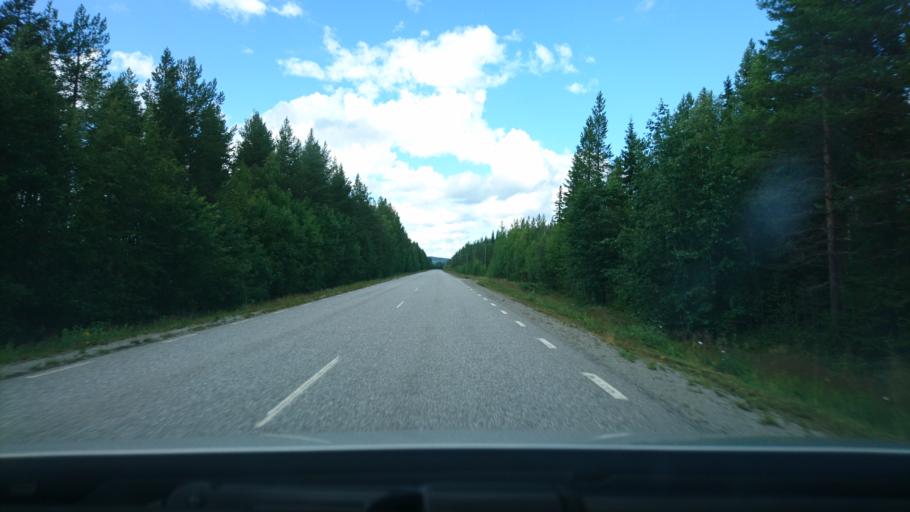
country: SE
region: Vaesterbotten
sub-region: Asele Kommun
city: Asele
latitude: 63.9840
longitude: 17.2653
